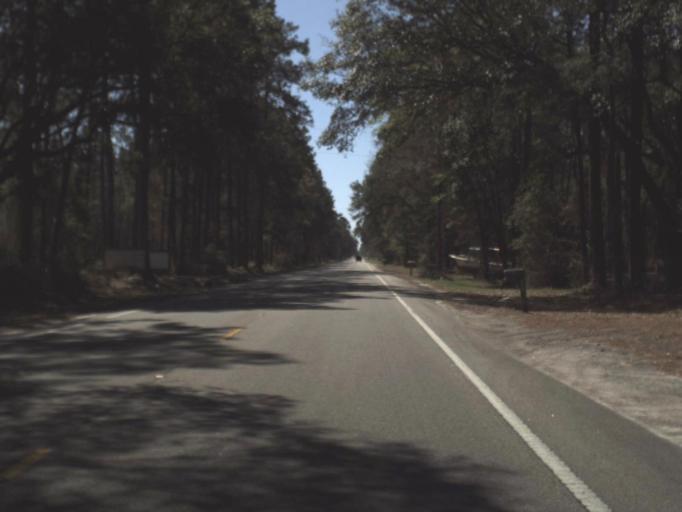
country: US
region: Florida
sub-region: Leon County
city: Woodville
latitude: 30.3210
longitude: -84.3116
